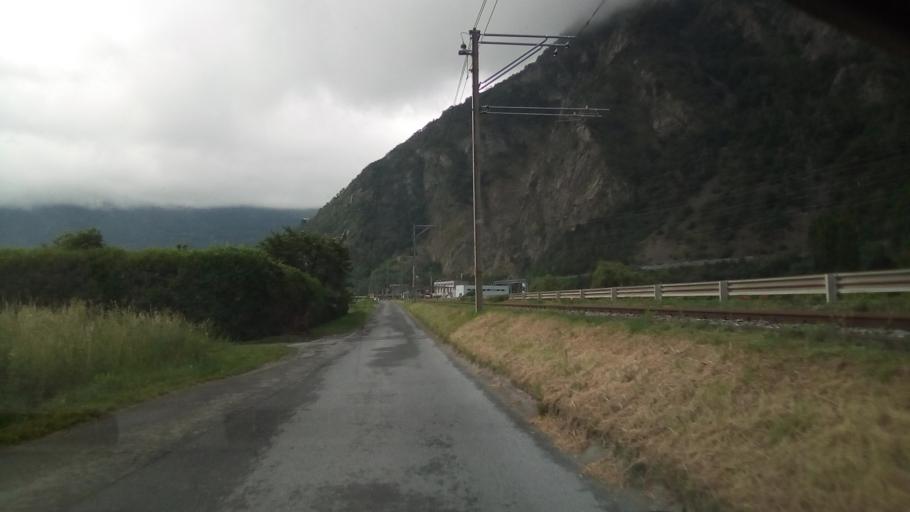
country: CH
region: Valais
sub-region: Martigny District
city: Martigny-Ville
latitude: 46.1150
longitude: 7.0577
